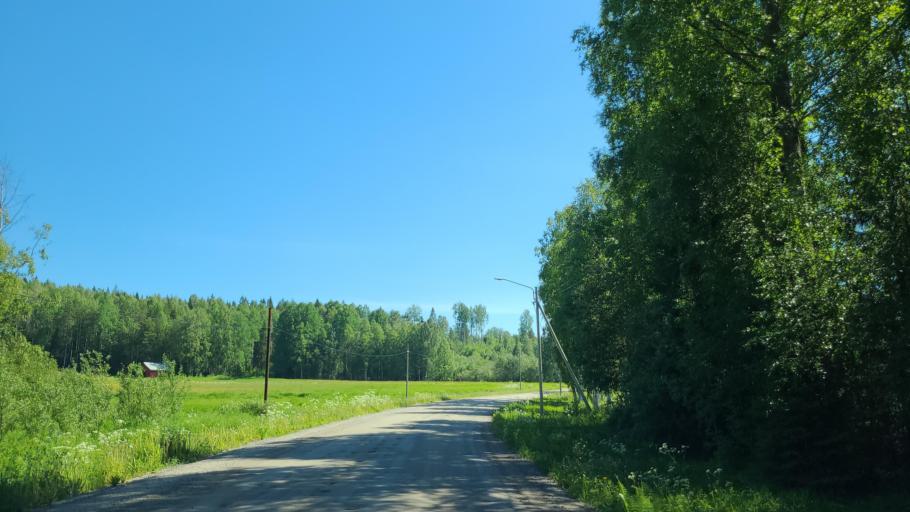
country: SE
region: Vaesterbotten
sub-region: Bjurholms Kommun
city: Bjurholm
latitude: 63.6944
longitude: 18.9567
